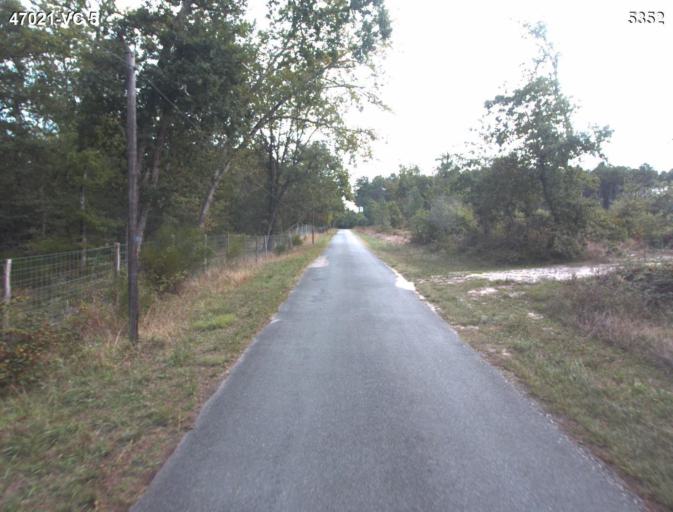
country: FR
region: Aquitaine
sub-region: Departement du Lot-et-Garonne
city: Barbaste
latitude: 44.1478
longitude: 0.2340
